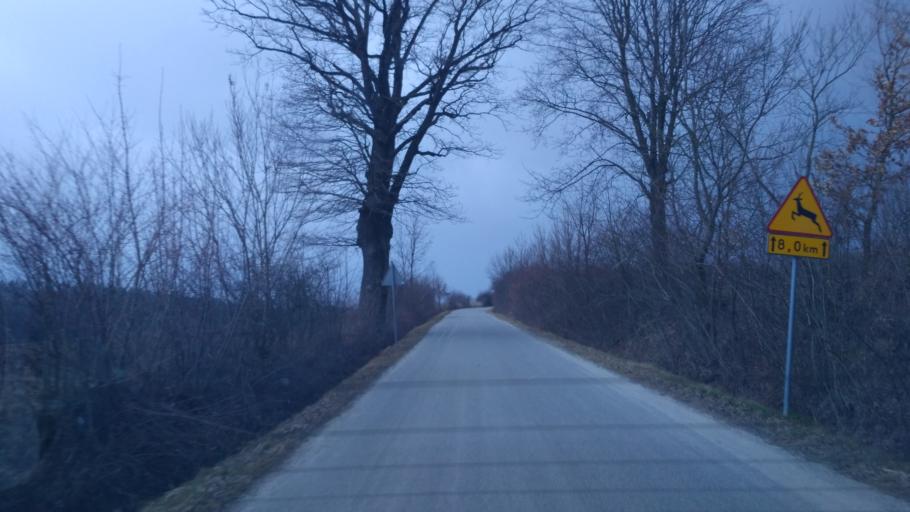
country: PL
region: Subcarpathian Voivodeship
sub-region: Powiat rzeszowski
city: Hyzne
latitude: 49.9019
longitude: 22.1955
